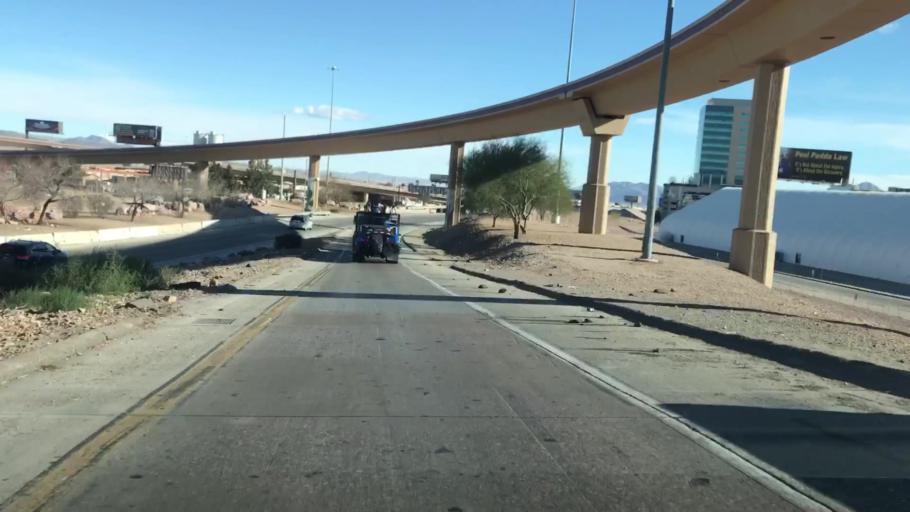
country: US
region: Nevada
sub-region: Clark County
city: Las Vegas
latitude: 36.1727
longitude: -115.1547
